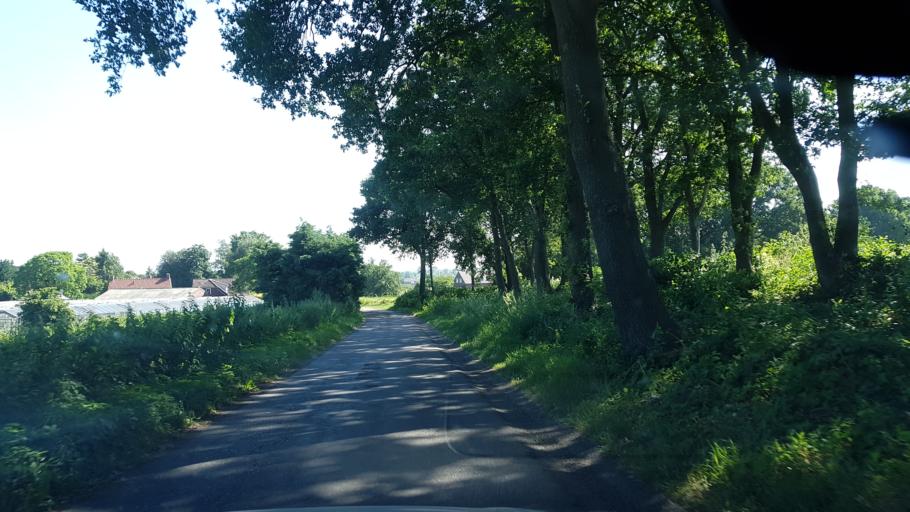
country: NL
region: Gelderland
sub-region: Gemeente Groesbeek
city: Bredeweg
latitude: 51.7526
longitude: 5.9349
